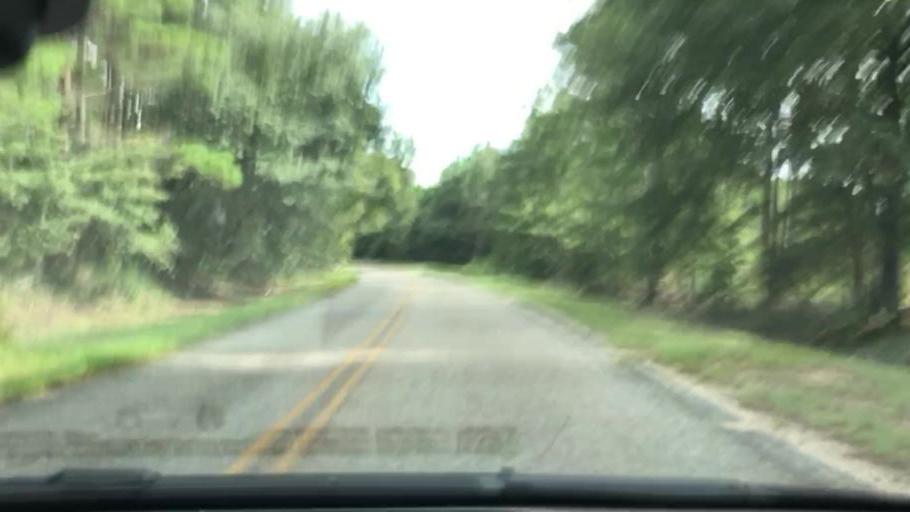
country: US
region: Georgia
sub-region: Early County
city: Blakely
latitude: 31.5100
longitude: -84.9517
